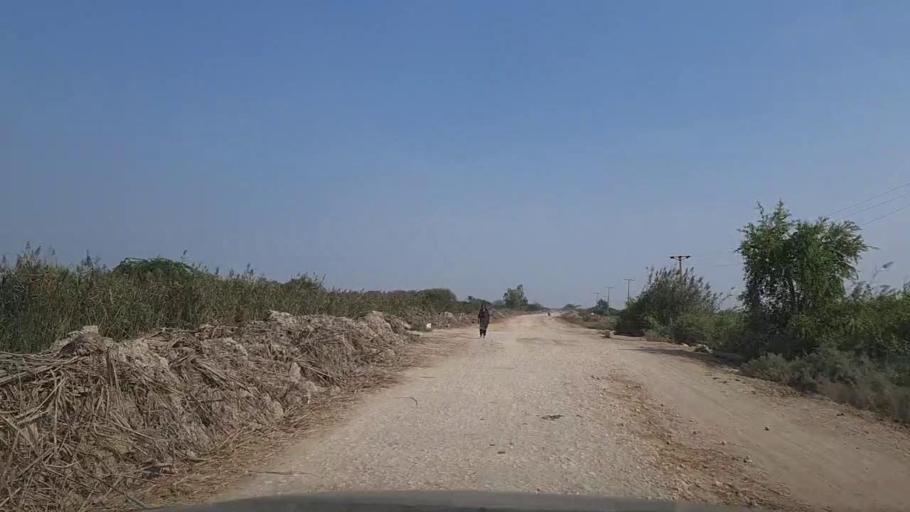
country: PK
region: Sindh
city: Thatta
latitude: 24.5830
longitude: 67.9029
